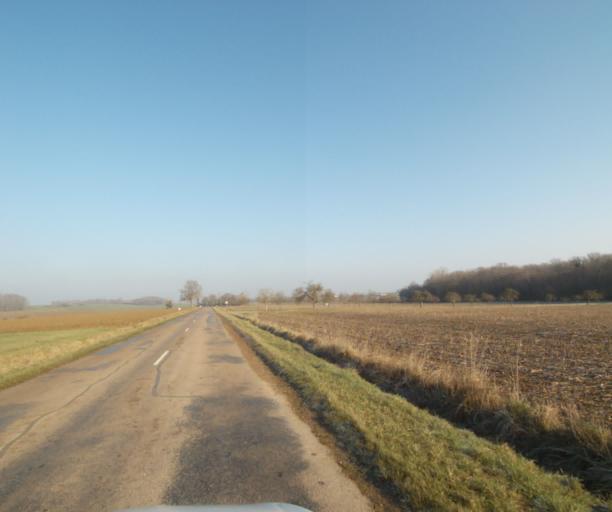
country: FR
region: Champagne-Ardenne
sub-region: Departement de la Haute-Marne
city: Montier-en-Der
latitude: 48.4399
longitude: 4.7566
